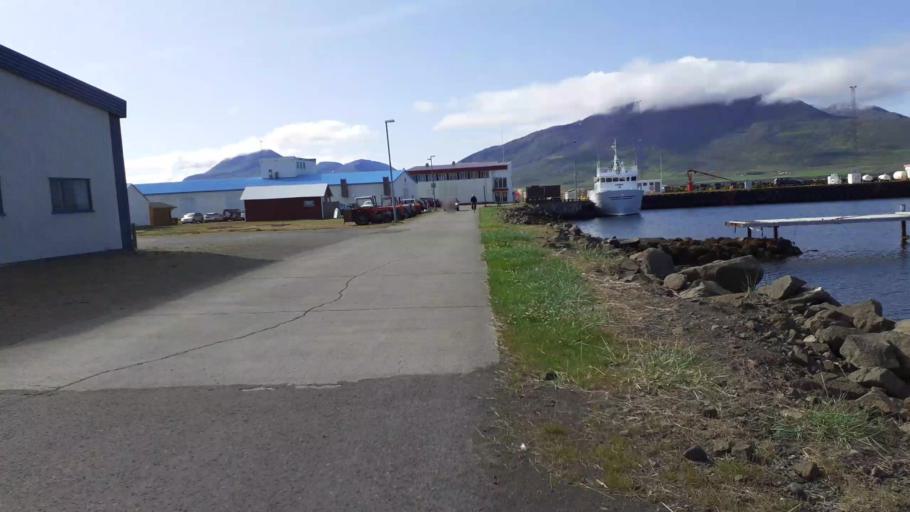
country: IS
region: Northeast
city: Dalvik
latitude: 65.9798
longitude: -18.3796
